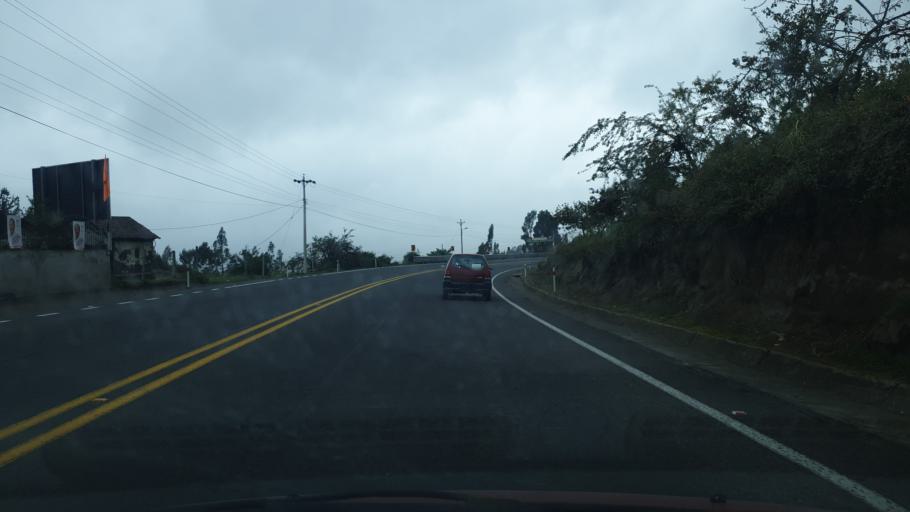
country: EC
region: Tungurahua
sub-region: Canton Quero
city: Quero
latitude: -1.3825
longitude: -78.6468
